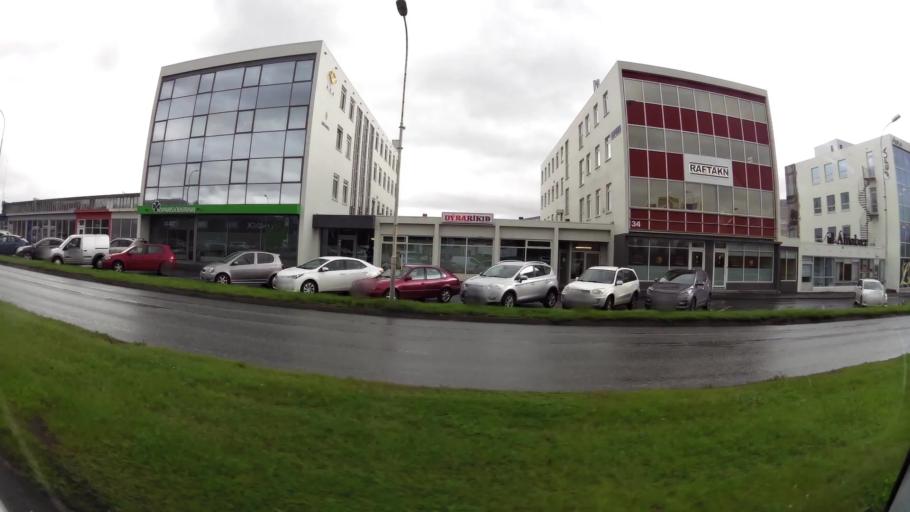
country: IS
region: Northeast
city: Akureyri
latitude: 65.6880
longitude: -18.0994
